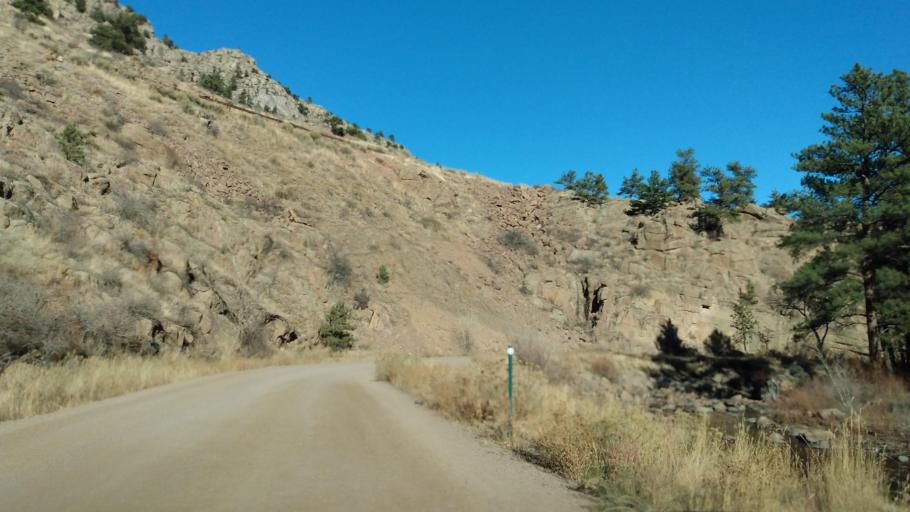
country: US
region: Colorado
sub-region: Boulder County
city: Lyons
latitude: 40.2365
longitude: -105.3226
